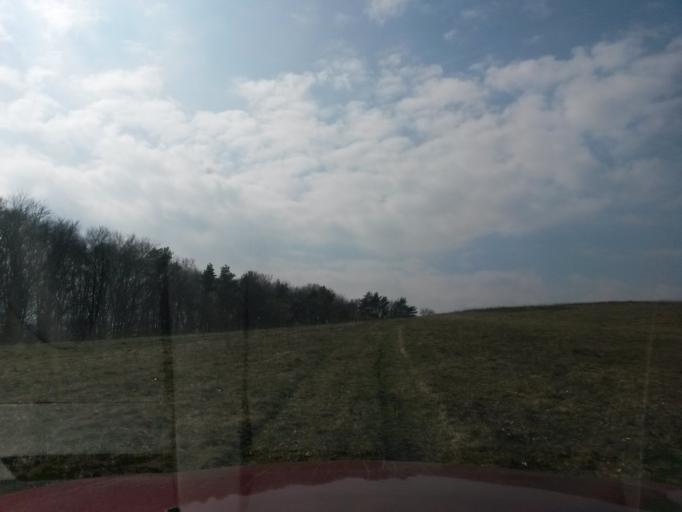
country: SK
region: Presovsky
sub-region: Okres Presov
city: Presov
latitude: 48.9299
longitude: 21.1523
